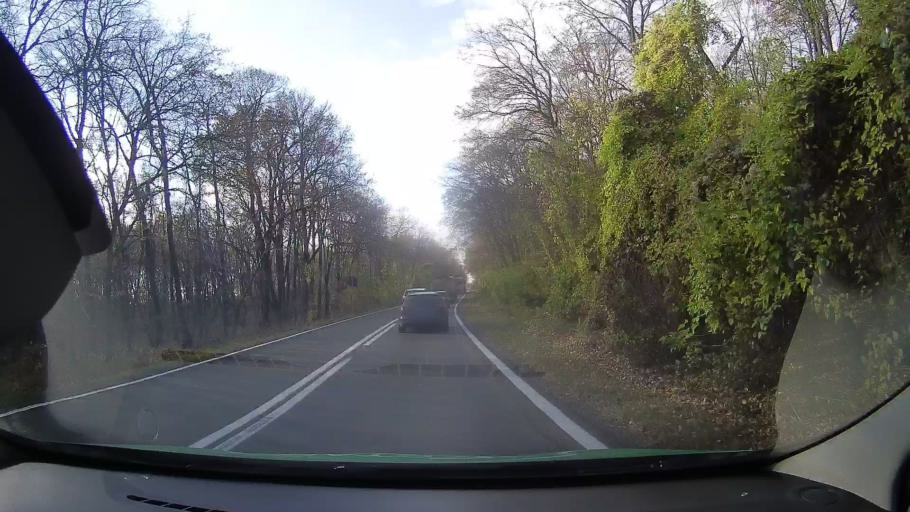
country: RO
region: Tulcea
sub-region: Comuna Topolog
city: Topolog
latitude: 44.9066
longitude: 28.4149
